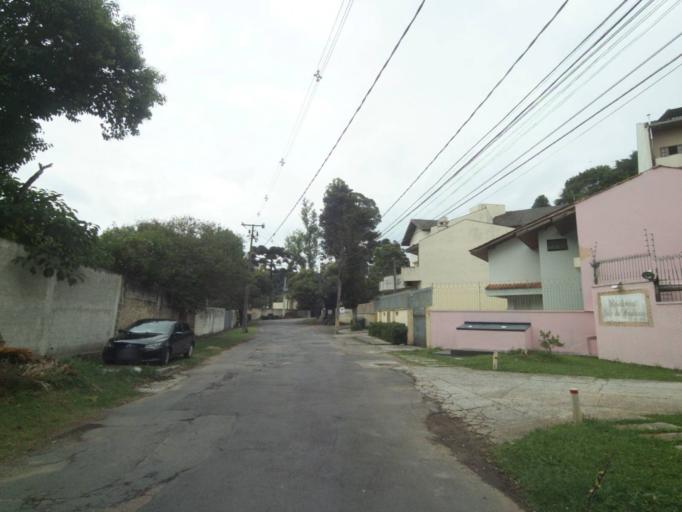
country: BR
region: Parana
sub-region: Curitiba
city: Curitiba
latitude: -25.4132
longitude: -49.3066
